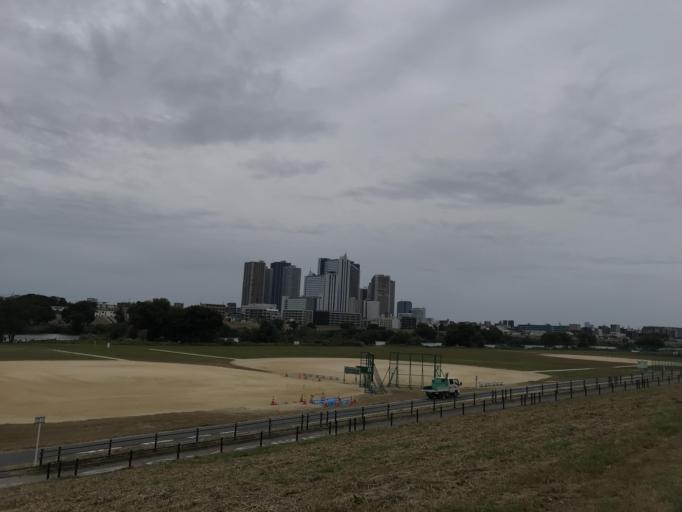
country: JP
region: Kanagawa
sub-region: Kawasaki-shi
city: Kawasaki
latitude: 35.5684
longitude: 139.6782
